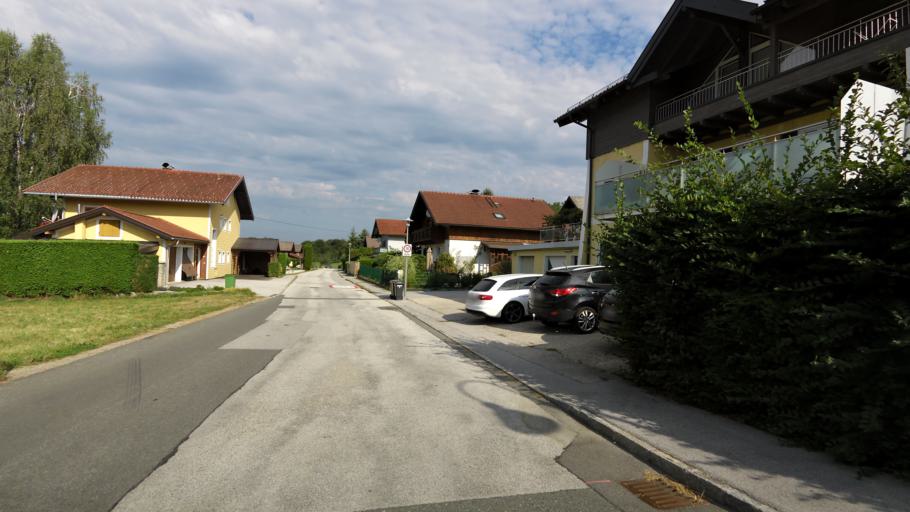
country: AT
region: Salzburg
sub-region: Politischer Bezirk Salzburg-Umgebung
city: Henndorf am Wallersee
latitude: 47.9048
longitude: 13.1927
